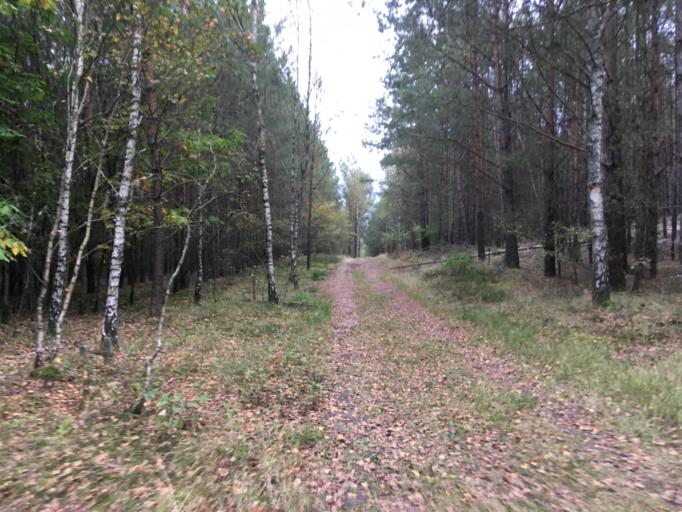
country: DE
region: Brandenburg
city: Birkenwerder
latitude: 52.7003
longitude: 13.3486
